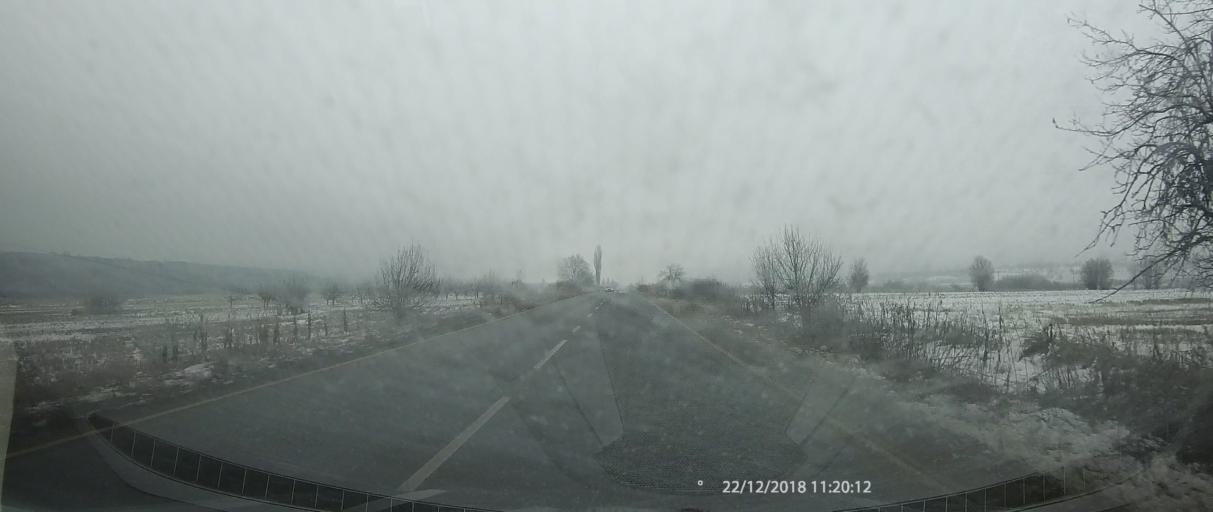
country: BG
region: Kyustendil
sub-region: Obshtina Kyustendil
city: Kyustendil
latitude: 42.2660
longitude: 22.8108
